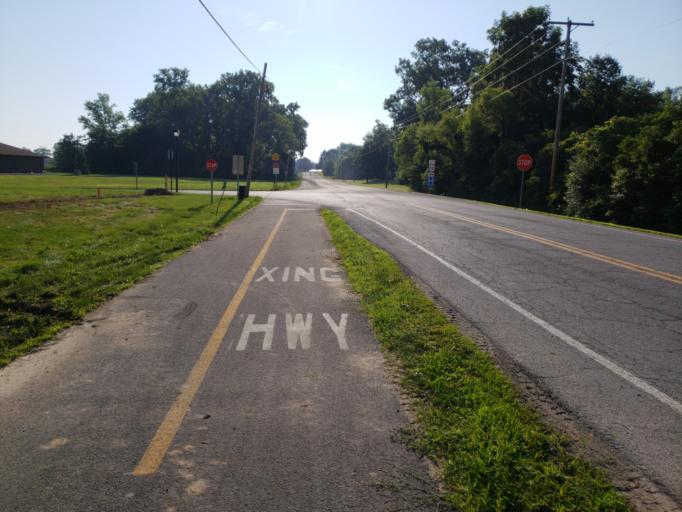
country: US
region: Ohio
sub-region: Huron County
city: Bellevue
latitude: 41.2835
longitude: -82.8844
